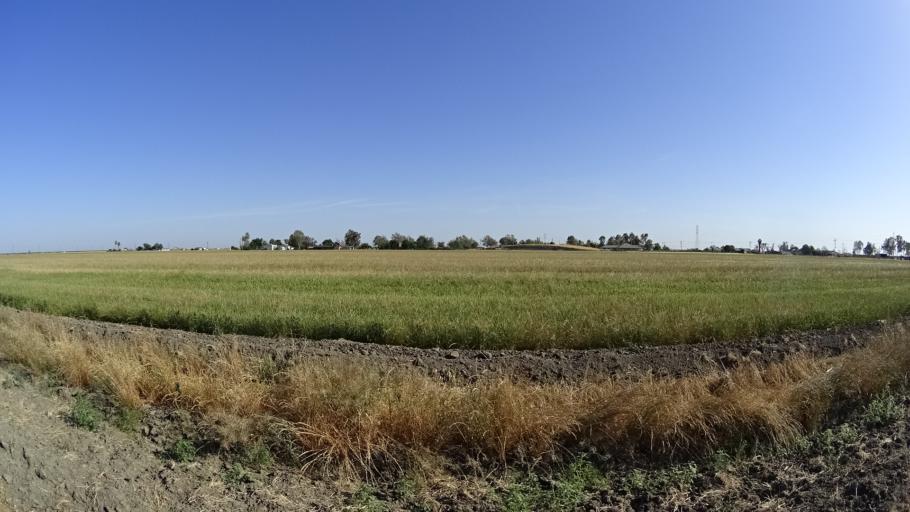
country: US
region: California
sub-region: Kings County
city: Corcoran
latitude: 36.1161
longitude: -119.5658
